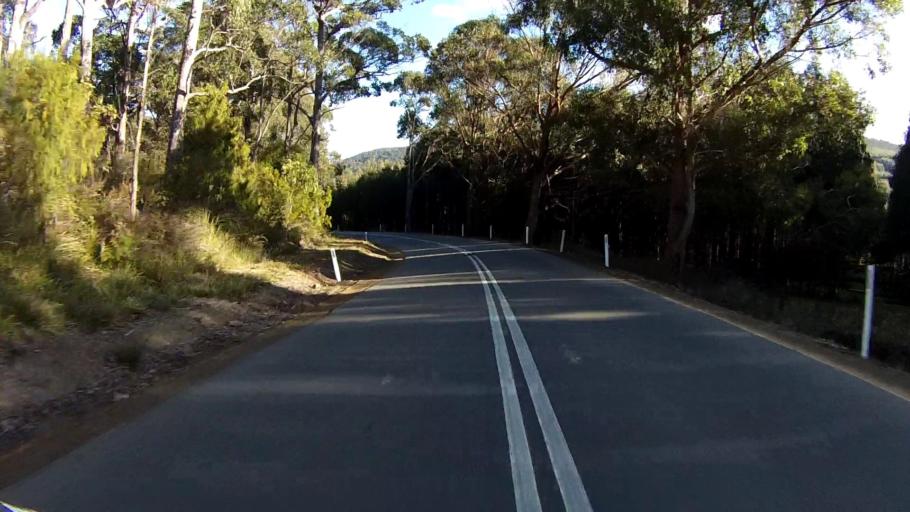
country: AU
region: Tasmania
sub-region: Clarence
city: Sandford
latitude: -43.1008
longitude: 147.8663
